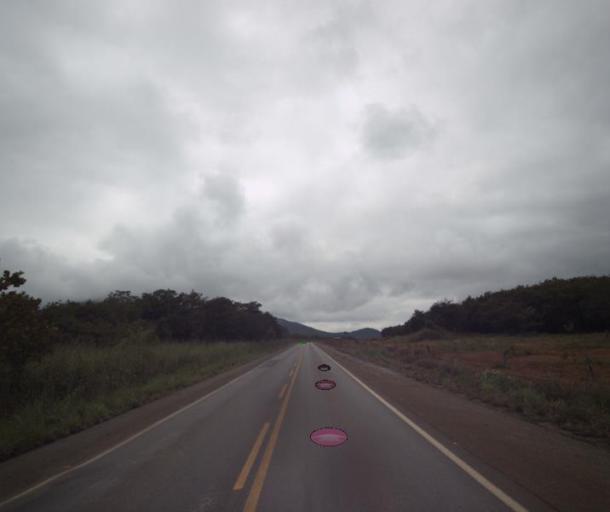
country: BR
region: Goias
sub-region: Barro Alto
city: Barro Alto
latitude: -14.8958
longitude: -48.9692
